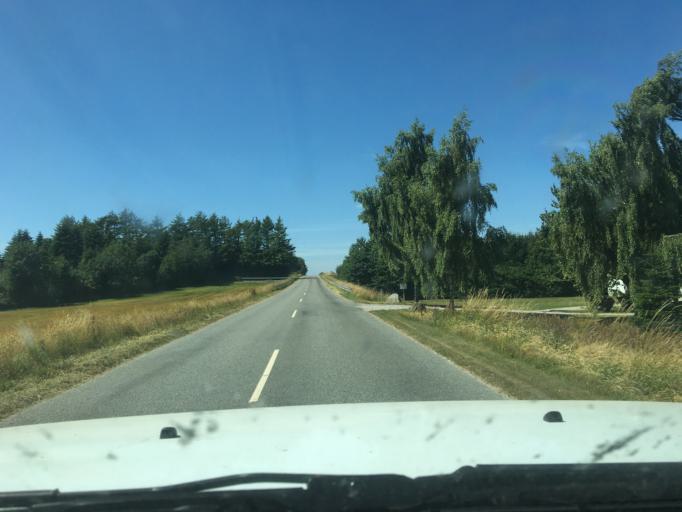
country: DK
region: Central Jutland
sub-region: Favrskov Kommune
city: Ulstrup
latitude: 56.4117
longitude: 9.7626
